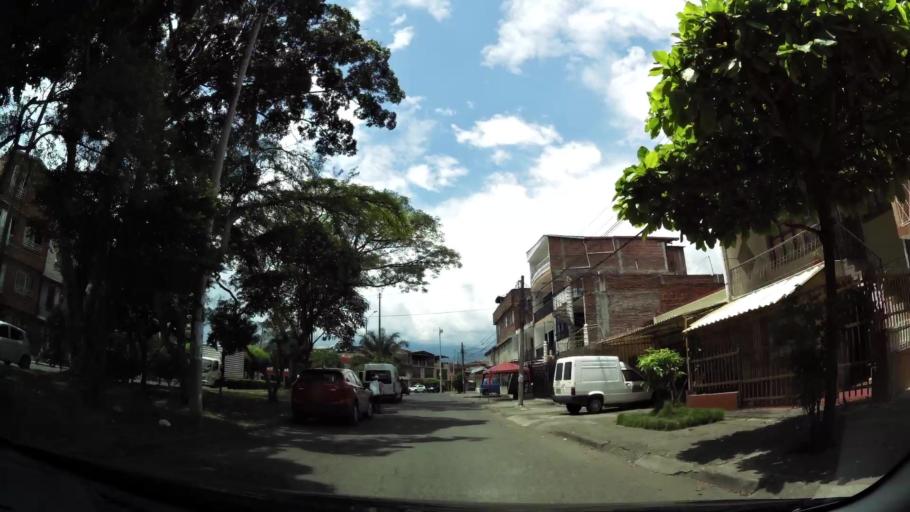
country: CO
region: Valle del Cauca
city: Cali
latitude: 3.4405
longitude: -76.5085
